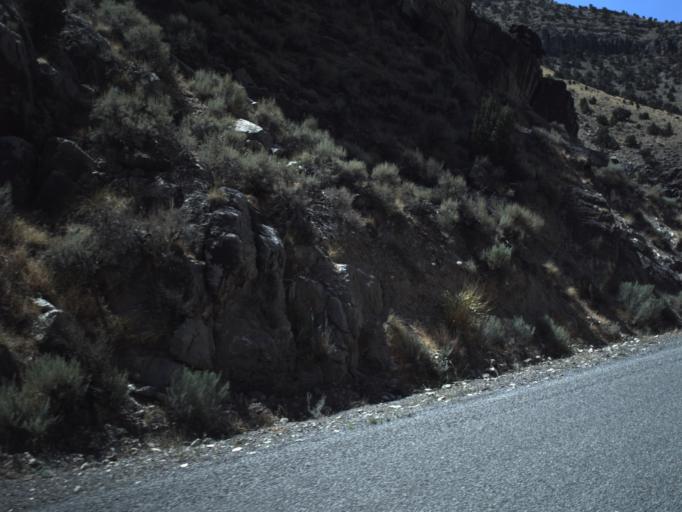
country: US
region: Utah
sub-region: Beaver County
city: Milford
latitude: 39.0860
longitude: -113.5688
